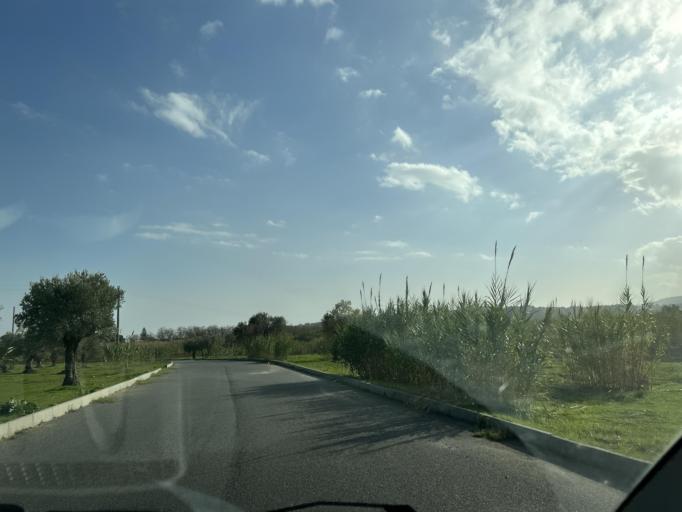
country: IT
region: Calabria
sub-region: Provincia di Catanzaro
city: Montepaone Lido
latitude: 38.7141
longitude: 16.5295
